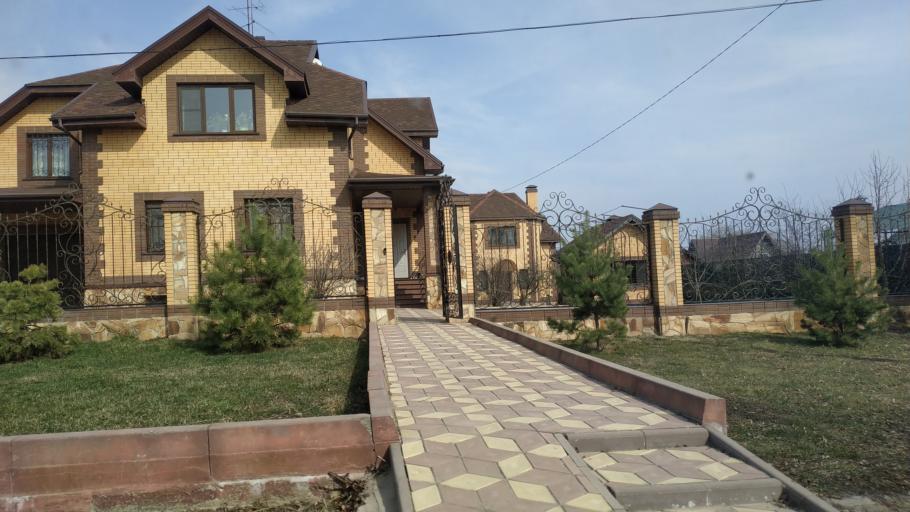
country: RU
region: Moskovskaya
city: Troitskoye
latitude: 55.3541
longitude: 38.4946
